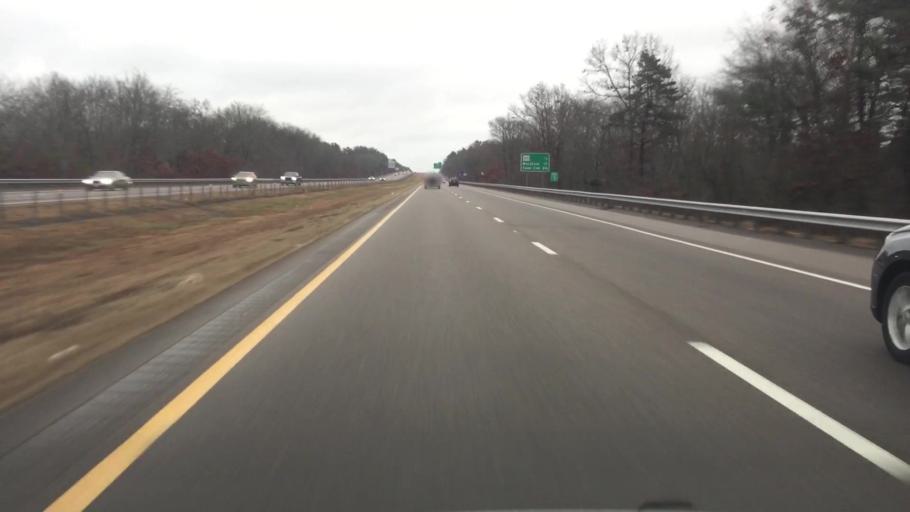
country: US
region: Massachusetts
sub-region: Plymouth County
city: Middleborough Center
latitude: 41.8906
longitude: -70.9411
